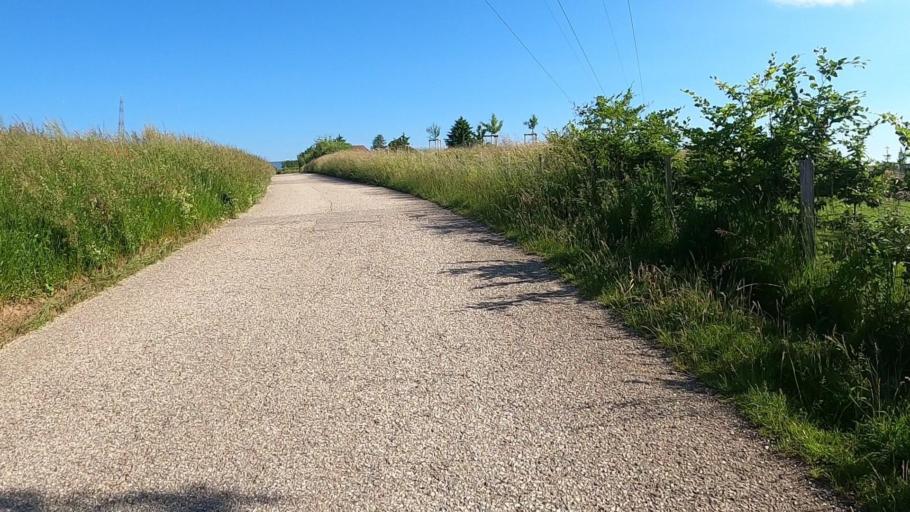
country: CH
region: Vaud
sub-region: Nyon District
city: Rolle
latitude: 46.4830
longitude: 6.3361
